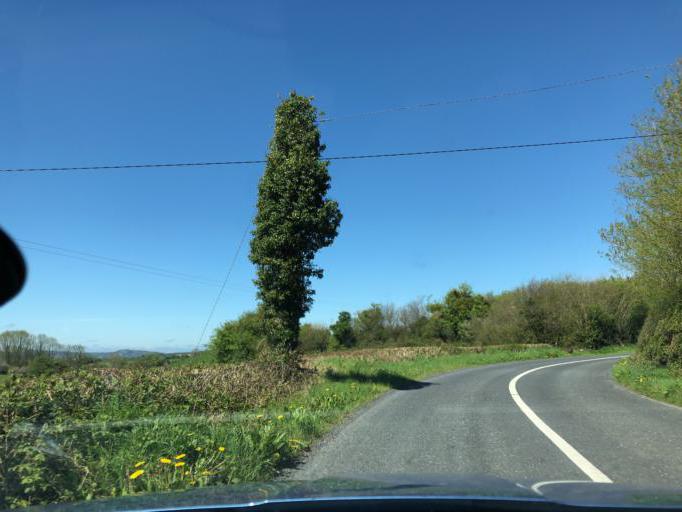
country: IE
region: Connaught
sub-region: County Galway
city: Loughrea
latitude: 53.1599
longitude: -8.3971
